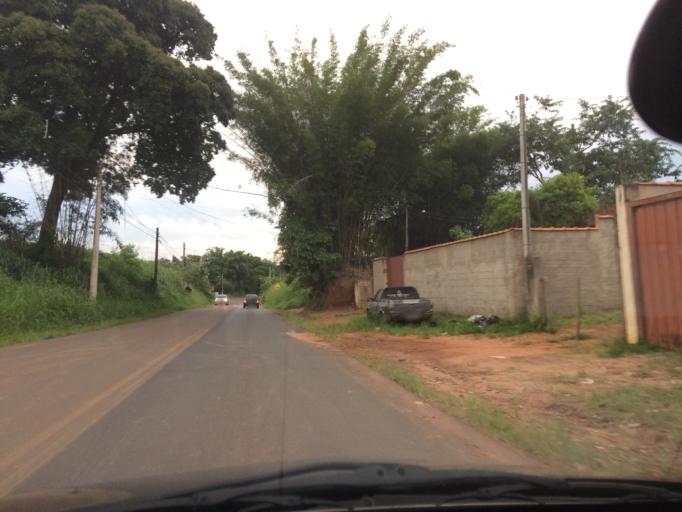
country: BR
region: Sao Paulo
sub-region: Casa Branca
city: Casa Branca
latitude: -21.7684
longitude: -47.0986
